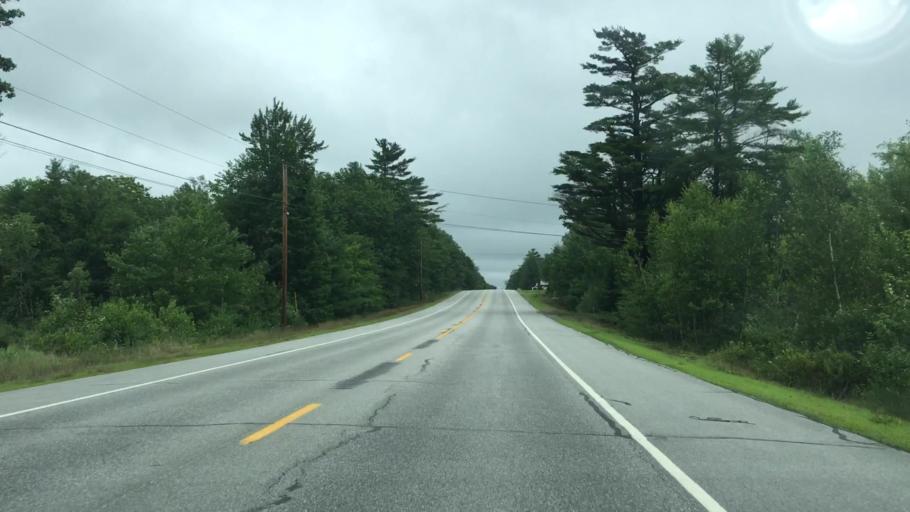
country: US
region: Maine
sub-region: Kennebec County
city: Windsor
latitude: 44.2761
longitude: -69.6396
